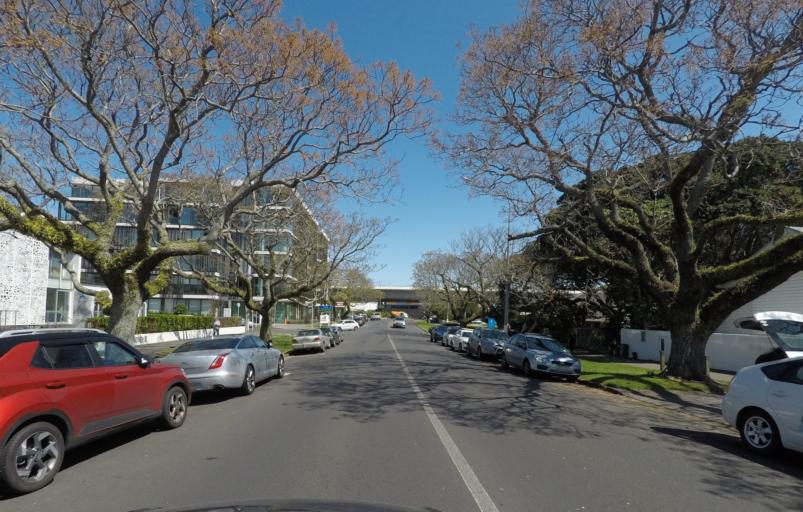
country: NZ
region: Auckland
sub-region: Auckland
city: Auckland
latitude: -36.8736
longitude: 174.7808
